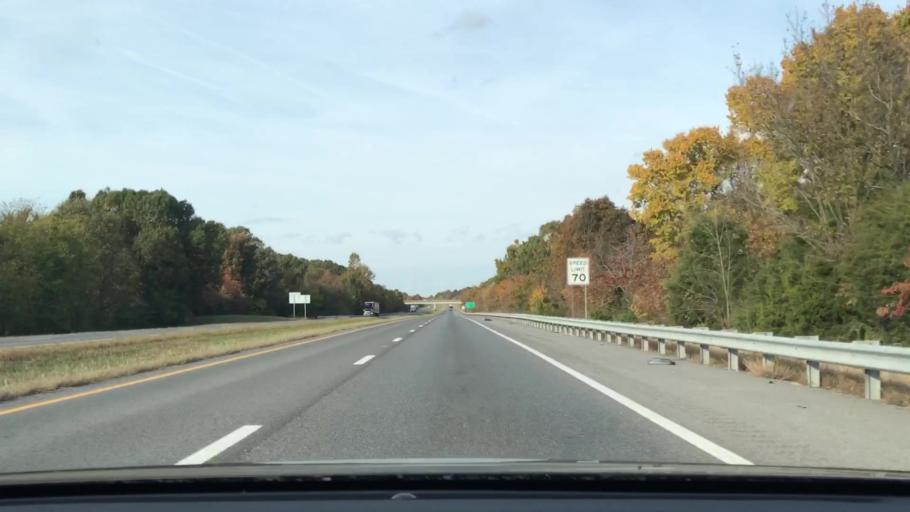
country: US
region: Kentucky
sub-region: Marshall County
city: Benton
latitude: 36.8478
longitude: -88.3863
